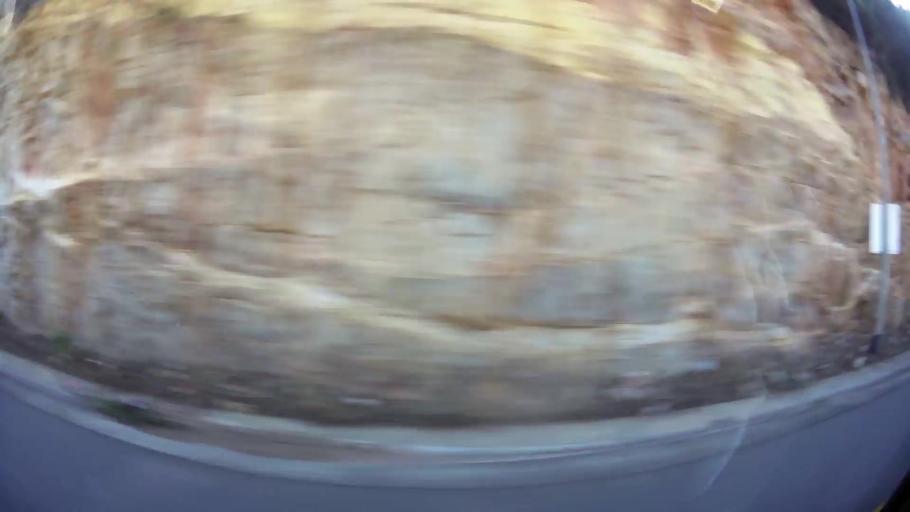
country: ZA
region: Western Cape
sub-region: Eden District Municipality
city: Knysna
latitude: -34.0376
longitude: 23.0218
